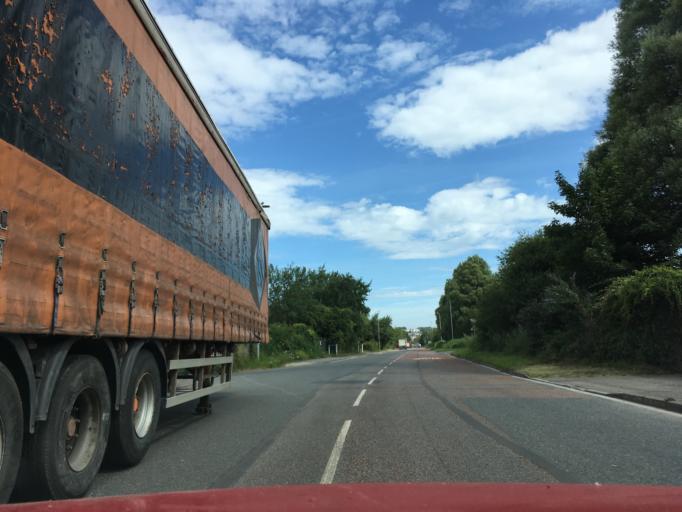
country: GB
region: Wales
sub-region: Newport
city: Nash
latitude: 51.5671
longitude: -2.9699
